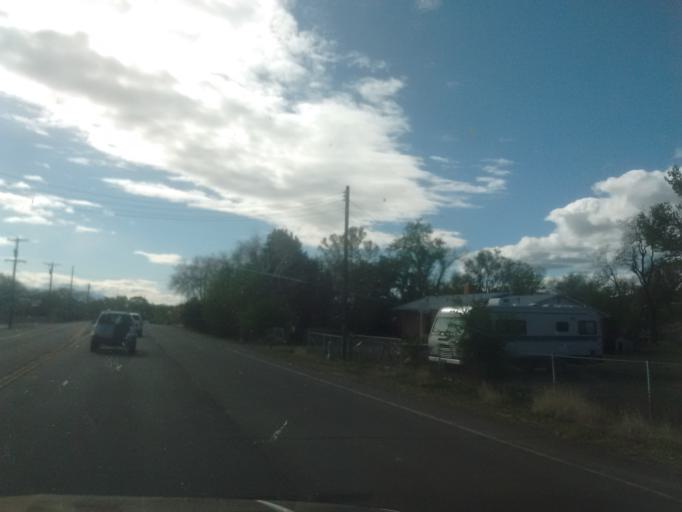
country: US
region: Colorado
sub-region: Mesa County
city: Redlands
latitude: 39.0806
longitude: -108.6381
